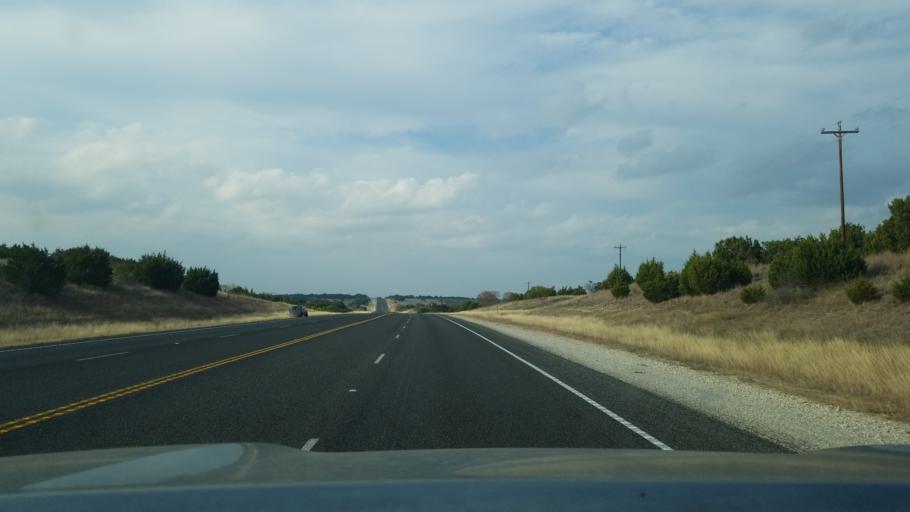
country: US
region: Texas
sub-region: Mills County
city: Goldthwaite
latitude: 31.3427
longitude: -98.5001
